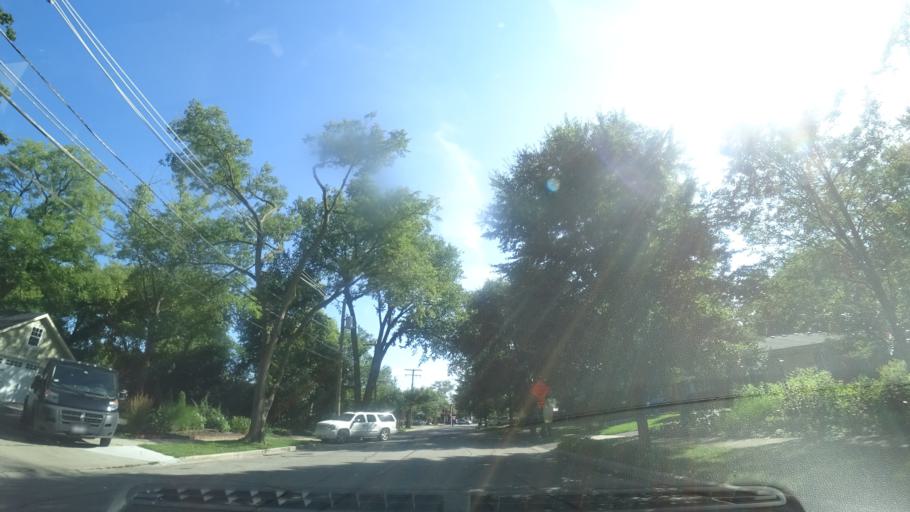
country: US
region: Illinois
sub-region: Cook County
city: Wilmette
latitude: 42.0540
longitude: -87.7095
